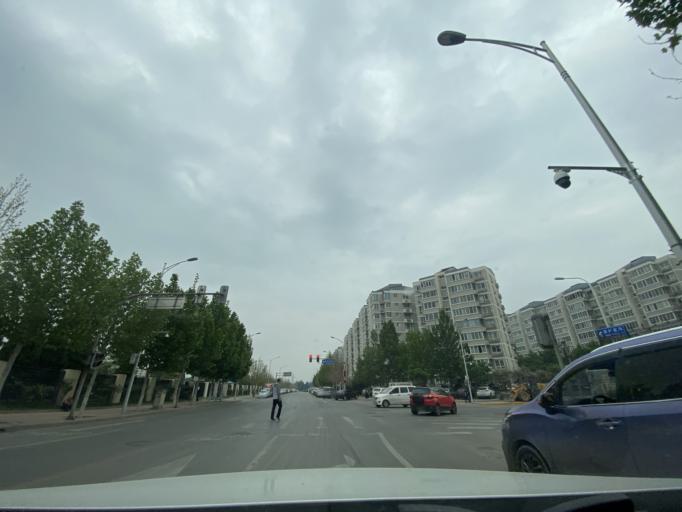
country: CN
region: Beijing
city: Sijiqing
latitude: 39.9329
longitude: 116.2417
